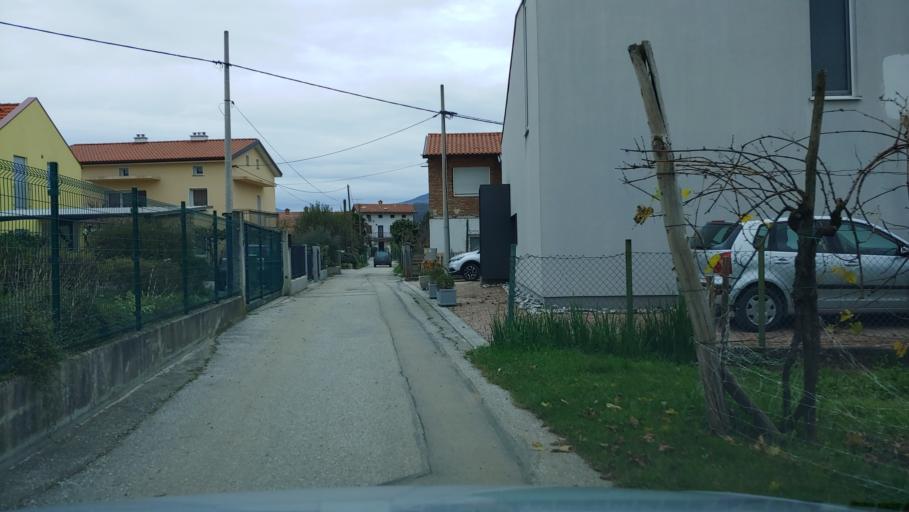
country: SI
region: Sempeter-Vrtojba
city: Vrtojba
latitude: 45.9130
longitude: 13.6393
